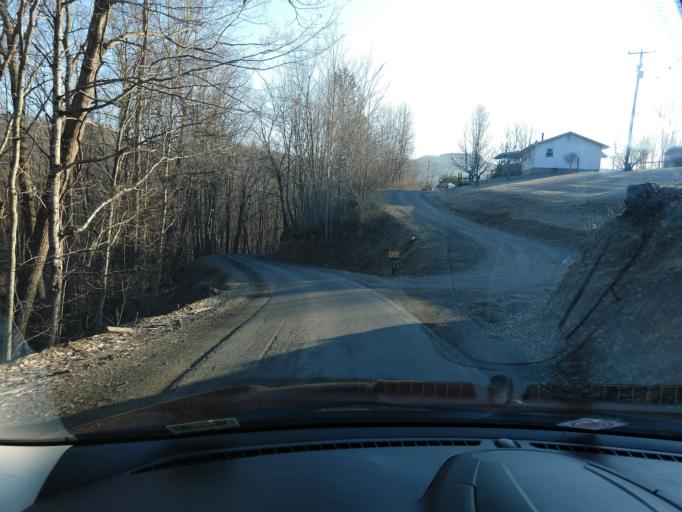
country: US
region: West Virginia
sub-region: Greenbrier County
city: Rainelle
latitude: 37.9244
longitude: -80.7384
